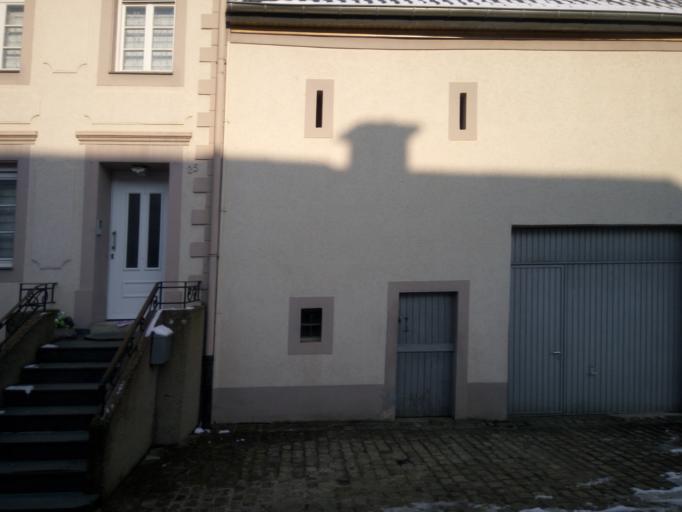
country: LU
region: Grevenmacher
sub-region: Canton d'Echternach
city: Consdorf
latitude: 49.7812
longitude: 6.3392
